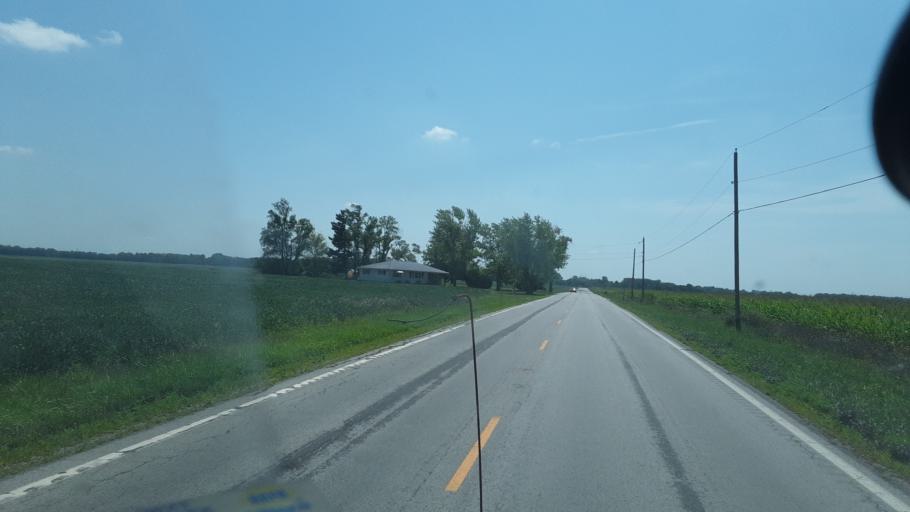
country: US
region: Ohio
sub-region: Hancock County
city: Arlington
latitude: 40.9344
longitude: -83.5679
